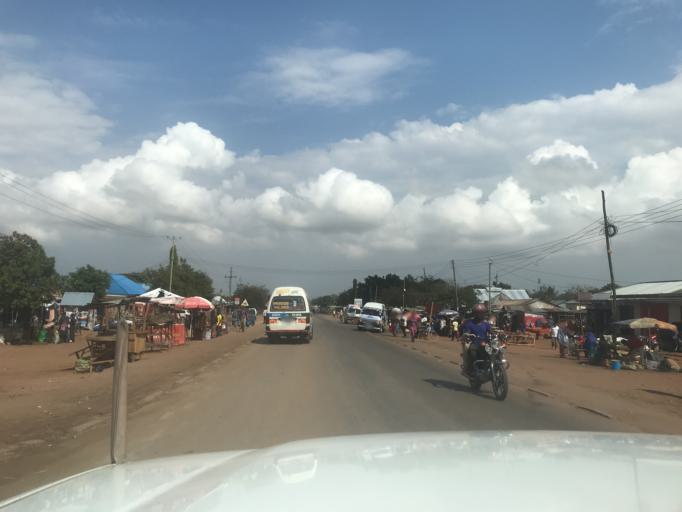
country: TZ
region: Mwanza
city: Usagara
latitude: -2.5554
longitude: 33.0471
